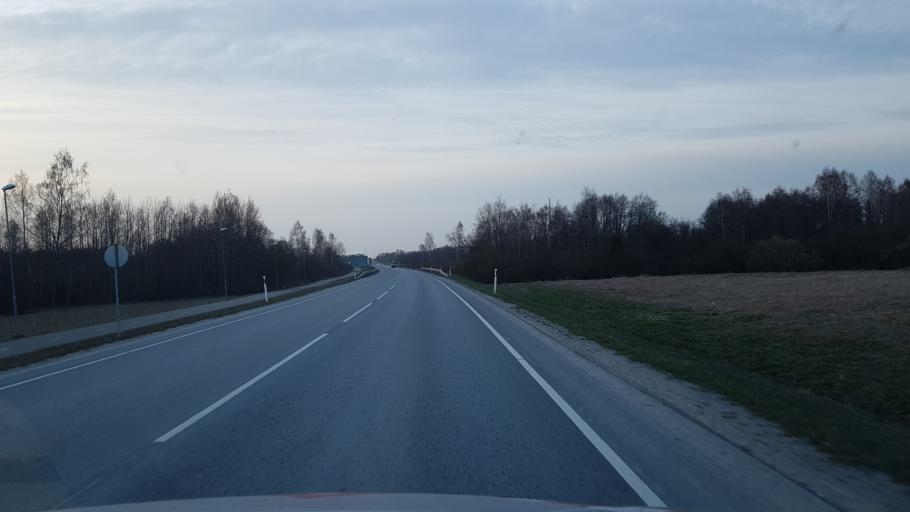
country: EE
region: Laeaene-Virumaa
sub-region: Rakvere linn
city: Rakvere
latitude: 59.3414
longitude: 26.3425
